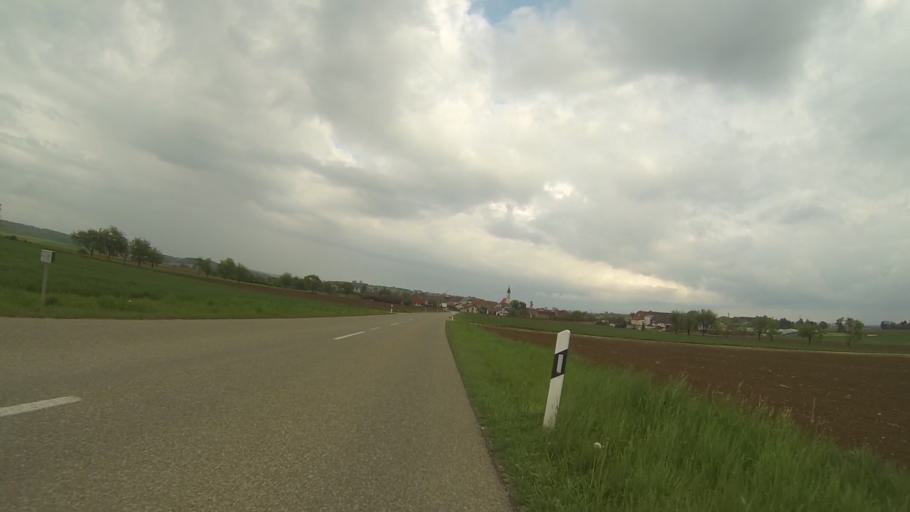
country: DE
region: Bavaria
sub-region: Swabia
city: Modingen
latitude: 48.6462
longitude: 10.4245
